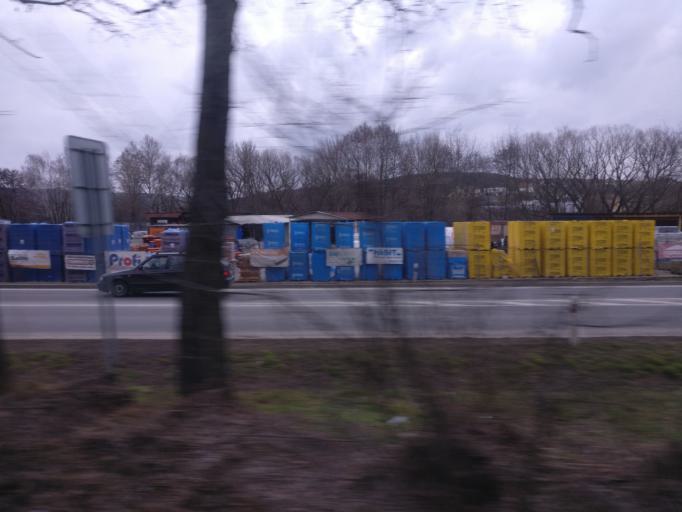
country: CZ
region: South Moravian
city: Zastavka
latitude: 49.1832
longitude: 16.3738
